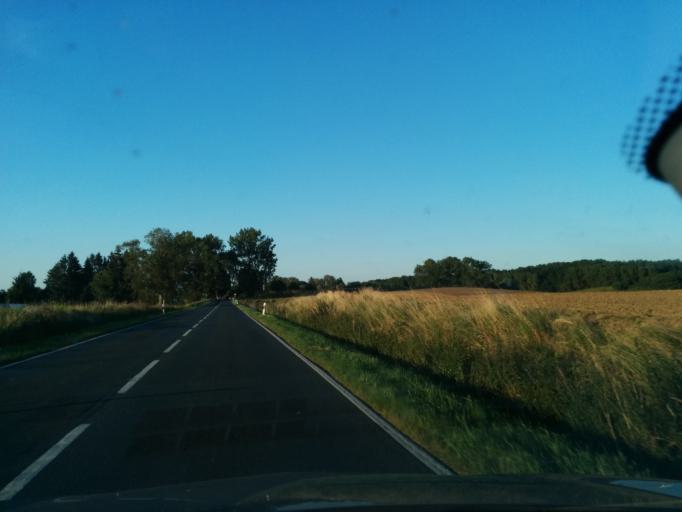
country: DE
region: Mecklenburg-Vorpommern
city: Loddin
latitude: 53.9337
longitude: 14.0359
